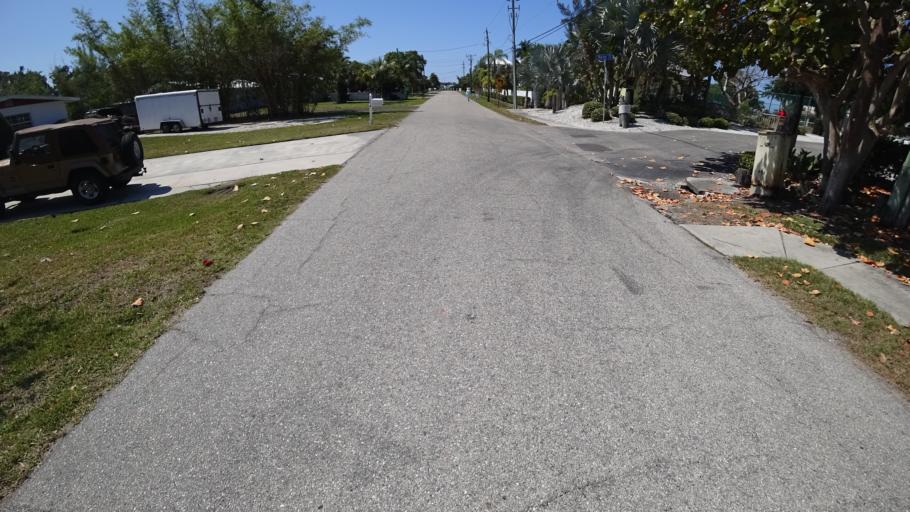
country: US
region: Florida
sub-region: Manatee County
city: Cortez
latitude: 27.4740
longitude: -82.6906
